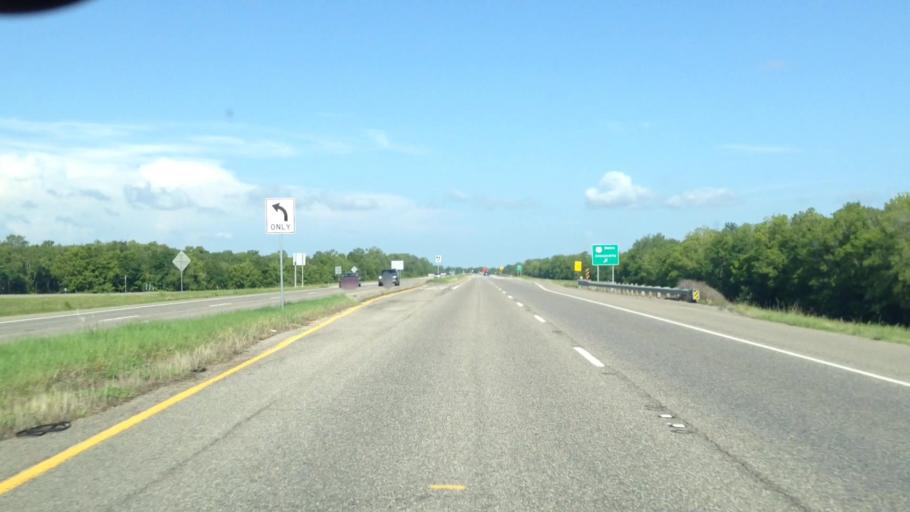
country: US
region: Louisiana
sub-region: Saint Landry Parish
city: Krotz Springs
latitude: 30.5451
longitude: -91.8087
